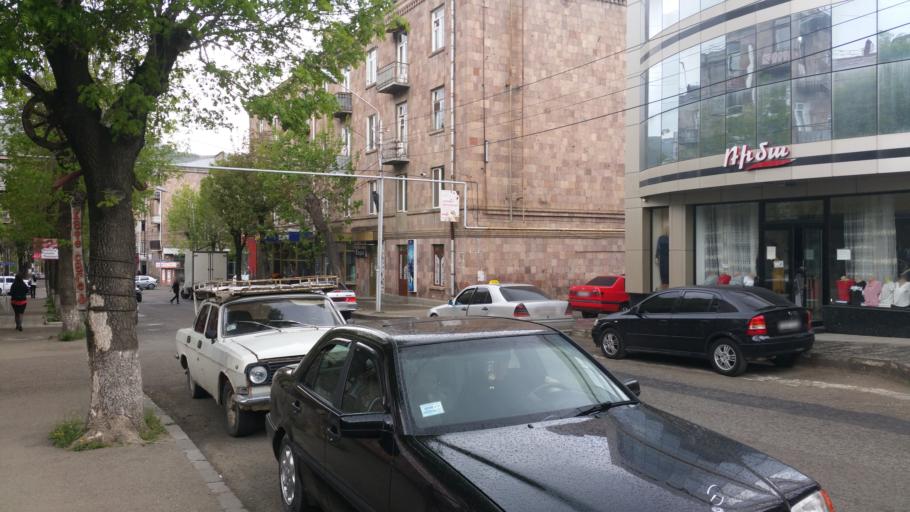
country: AM
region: Lorri
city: Vanadzor
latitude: 40.8098
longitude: 44.4874
